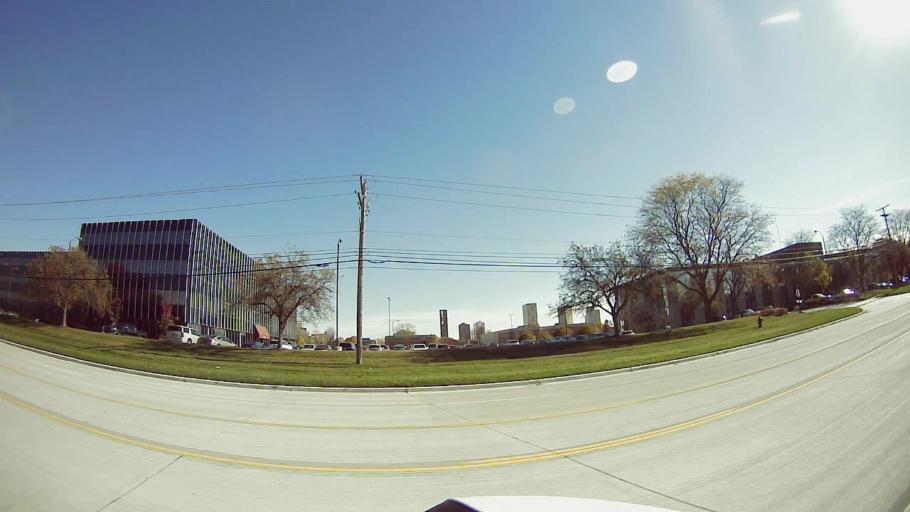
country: US
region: Michigan
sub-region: Oakland County
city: Bingham Farms
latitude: 42.4810
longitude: -83.2612
